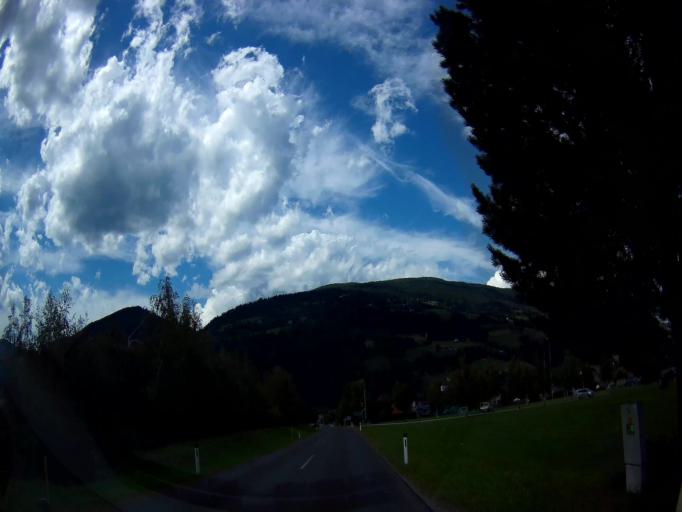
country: AT
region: Styria
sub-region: Politischer Bezirk Murau
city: Stadl an der Mur
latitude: 47.0807
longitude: 13.9816
